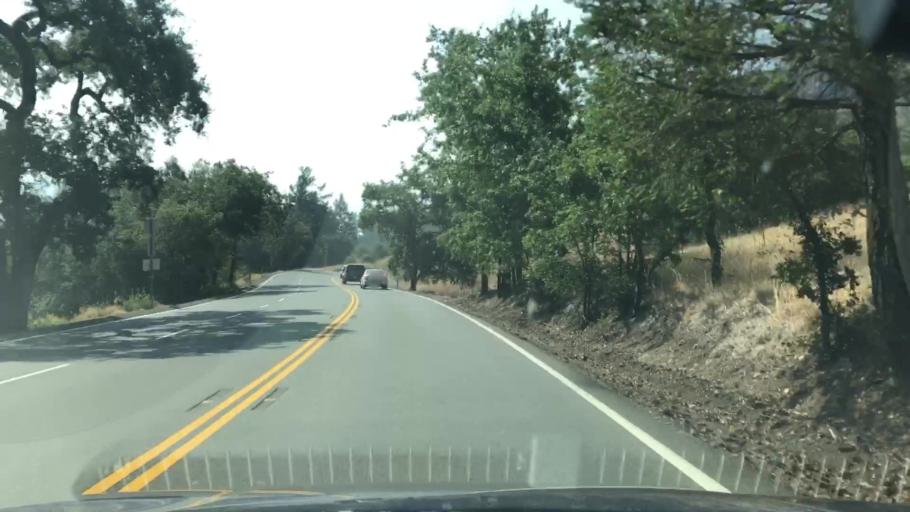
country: US
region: California
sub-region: Napa County
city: Calistoga
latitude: 38.6301
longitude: -122.6032
